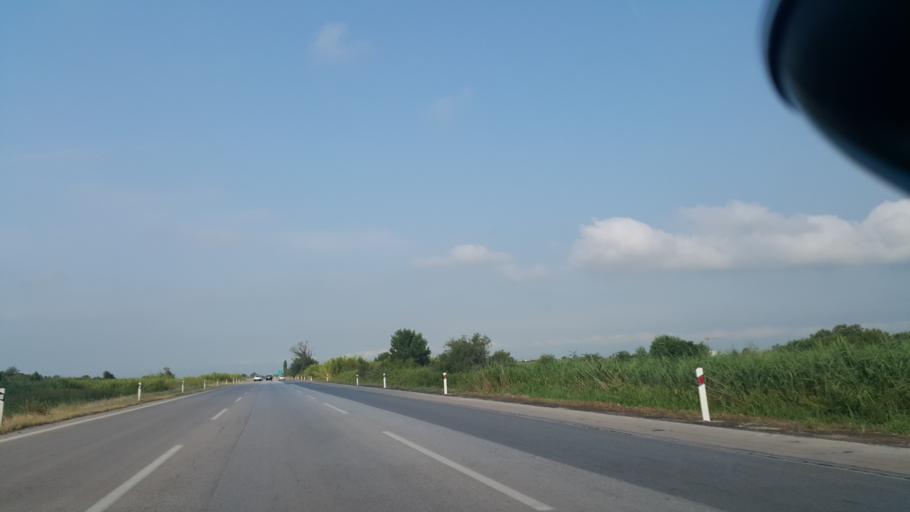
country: GR
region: Central Macedonia
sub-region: Nomos Thessalonikis
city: Chalastra
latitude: 40.6305
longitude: 22.7747
